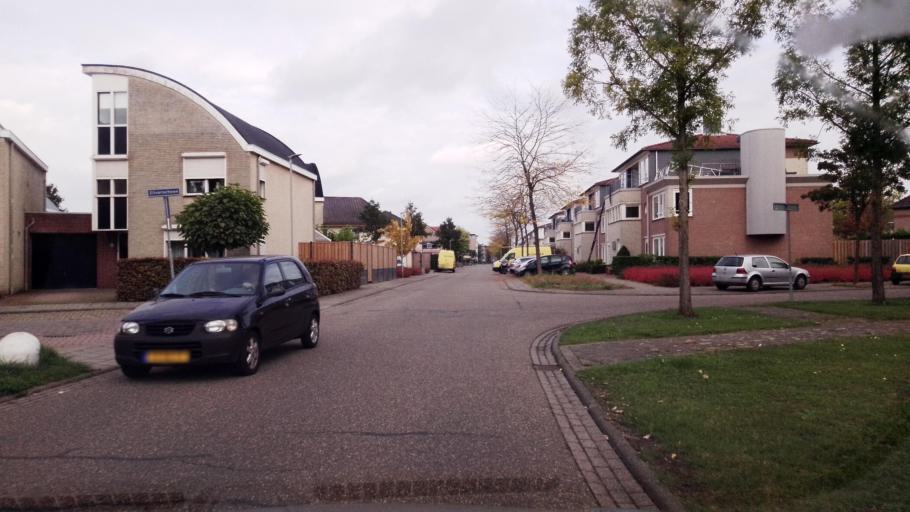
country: NL
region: Limburg
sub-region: Gemeente Venlo
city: Tegelen
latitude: 51.3423
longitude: 6.1269
